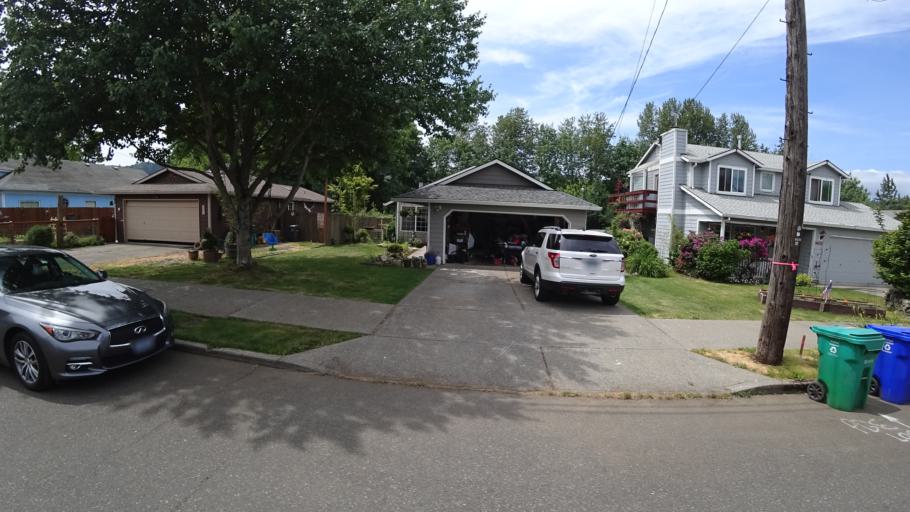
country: US
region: Oregon
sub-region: Washington County
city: West Haven
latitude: 45.5944
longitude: -122.7640
